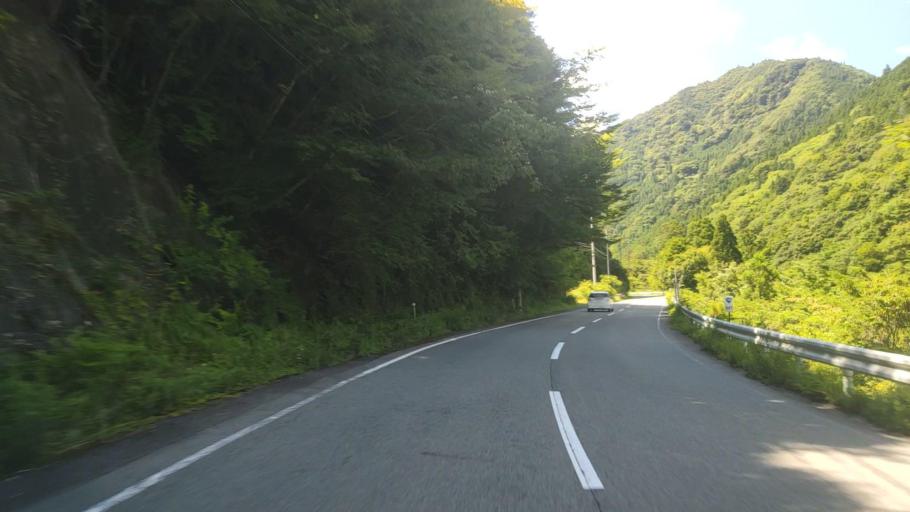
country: JP
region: Mie
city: Owase
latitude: 34.1863
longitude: 135.9981
